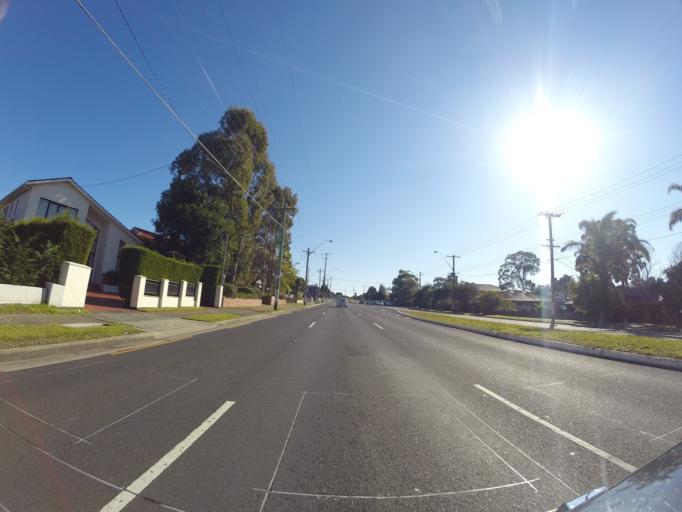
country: AU
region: New South Wales
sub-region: Kogarah
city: Blakehurst
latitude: -33.9843
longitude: 151.1093
